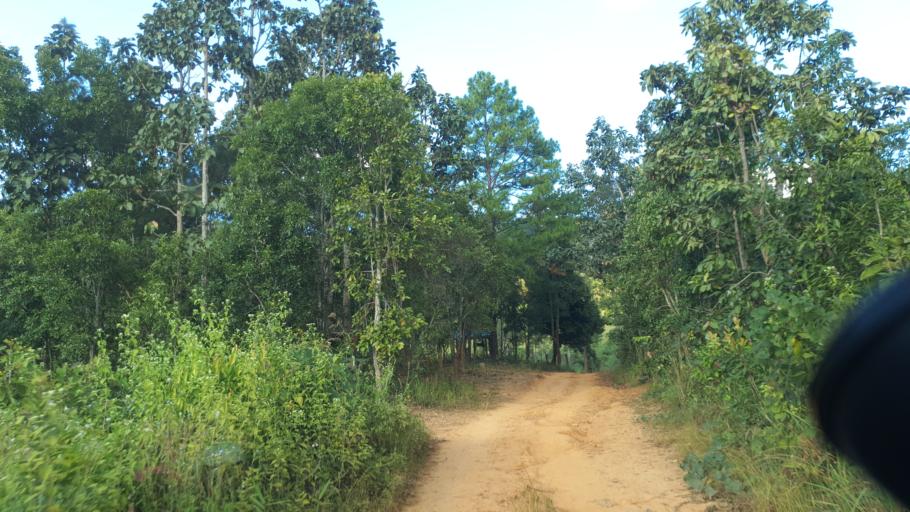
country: TH
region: Chiang Mai
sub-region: Amphoe Chiang Dao
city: Chiang Dao
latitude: 19.4041
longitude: 98.8306
